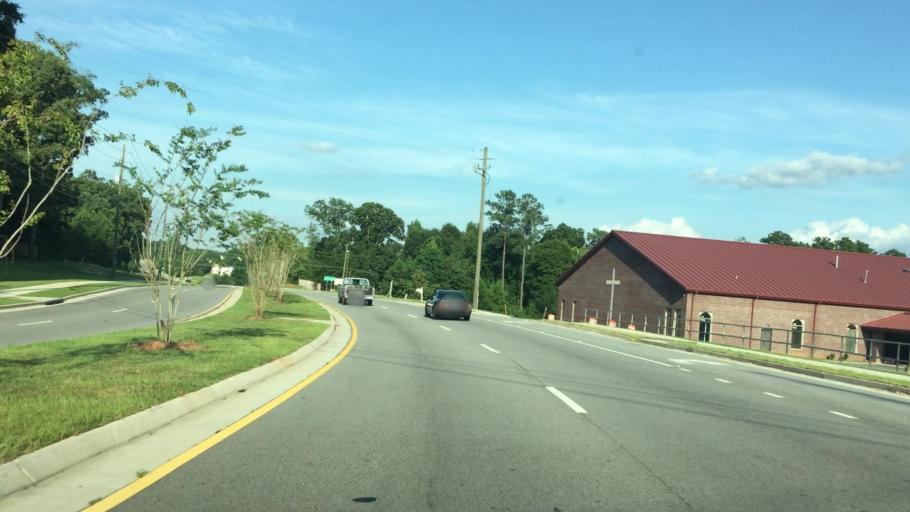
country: US
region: Georgia
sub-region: Clayton County
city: Lake City
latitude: 33.6102
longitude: -84.2845
